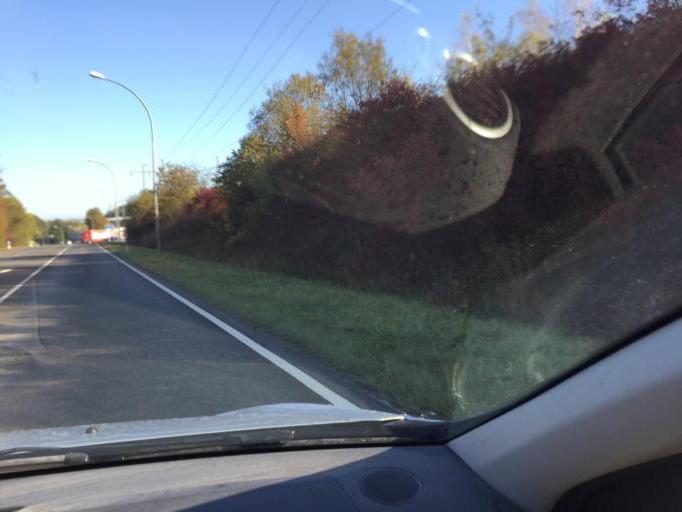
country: LU
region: Luxembourg
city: Colmar
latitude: 49.7995
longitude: 6.0993
